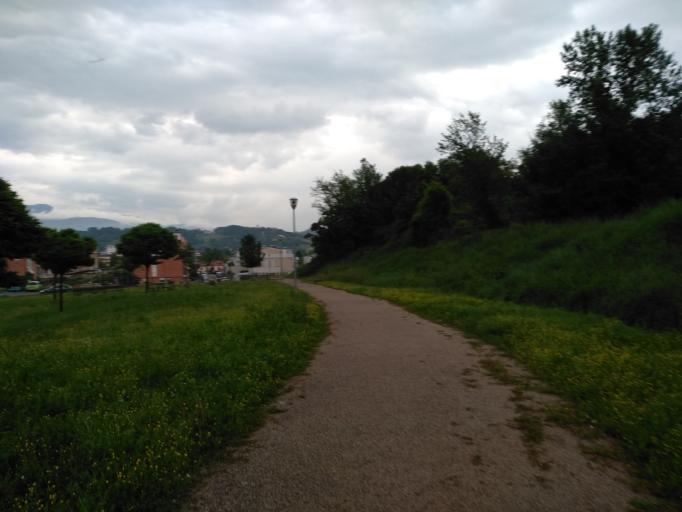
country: IT
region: Tuscany
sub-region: Province of Arezzo
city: San Giovanni Valdarno
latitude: 43.5581
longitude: 11.5267
